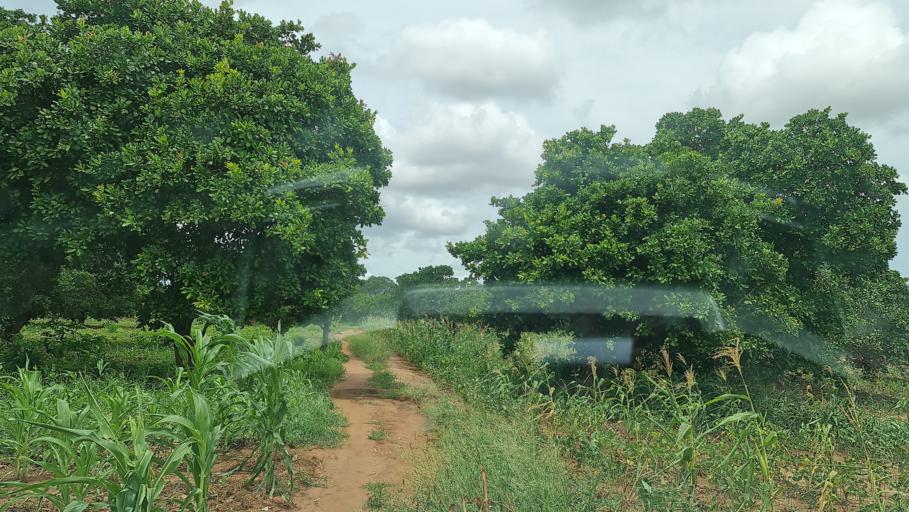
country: MZ
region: Nampula
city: Nacala
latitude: -14.7788
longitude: 39.9901
